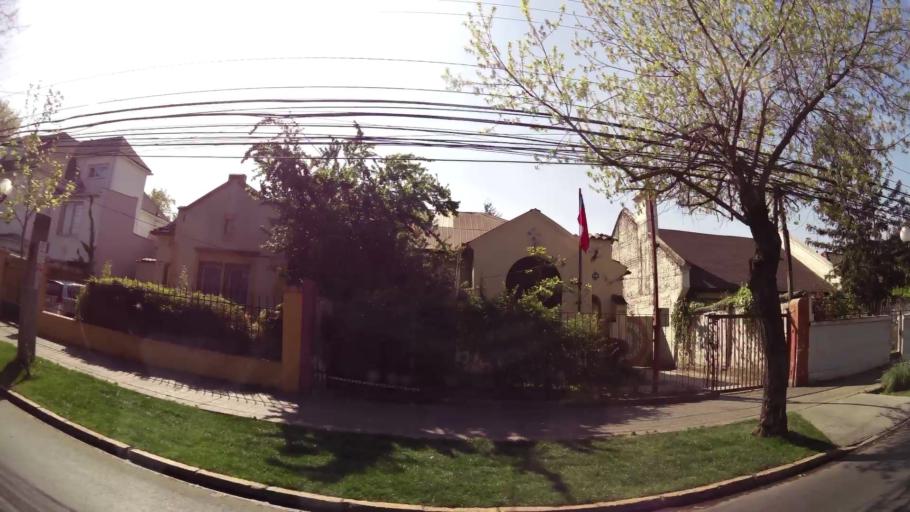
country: CL
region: Santiago Metropolitan
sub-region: Provincia de Santiago
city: Santiago
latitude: -33.4453
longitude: -70.6208
